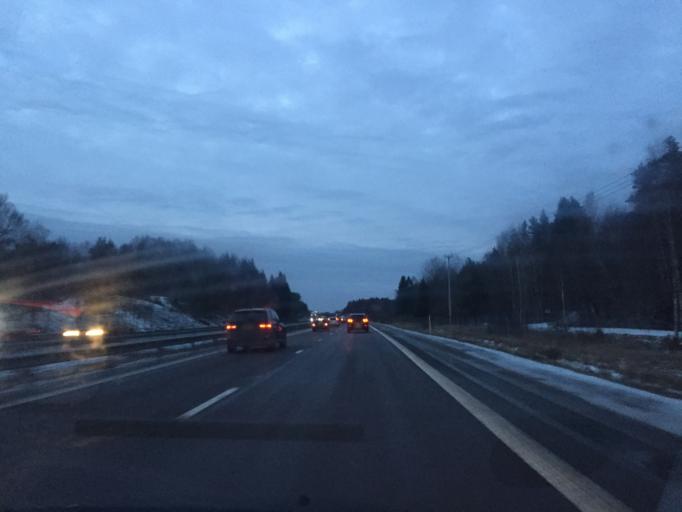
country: SE
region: Vaestra Goetaland
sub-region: Kungalvs Kommun
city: Kode
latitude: 57.9555
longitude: 11.8496
